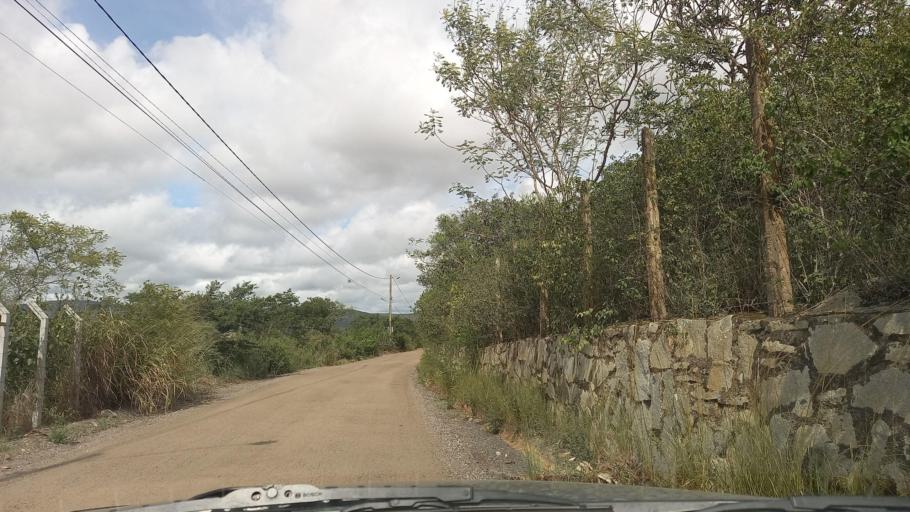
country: BR
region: Pernambuco
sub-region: Gravata
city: Gravata
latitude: -8.1810
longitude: -35.5762
